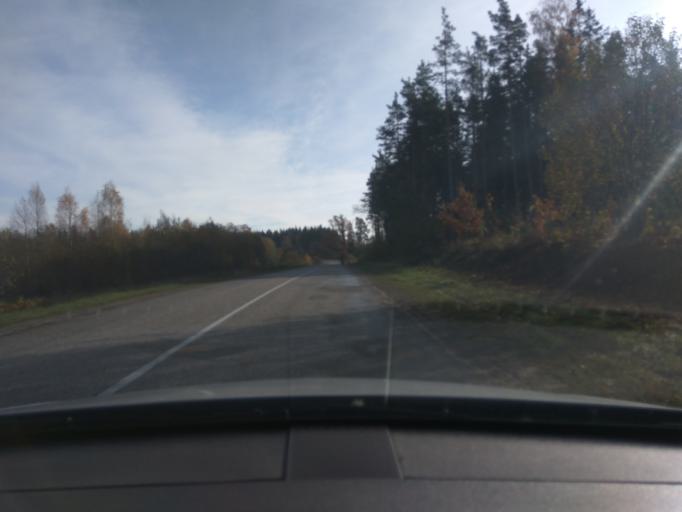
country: LV
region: Alsunga
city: Alsunga
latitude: 57.0090
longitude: 21.7170
